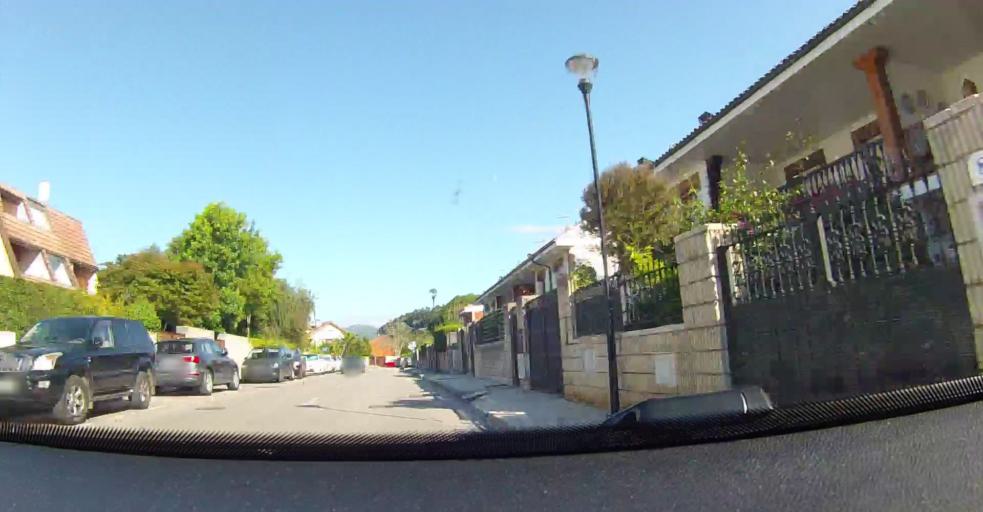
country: ES
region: Asturias
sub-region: Province of Asturias
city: Ribadesella
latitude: 43.4661
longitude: -5.0762
